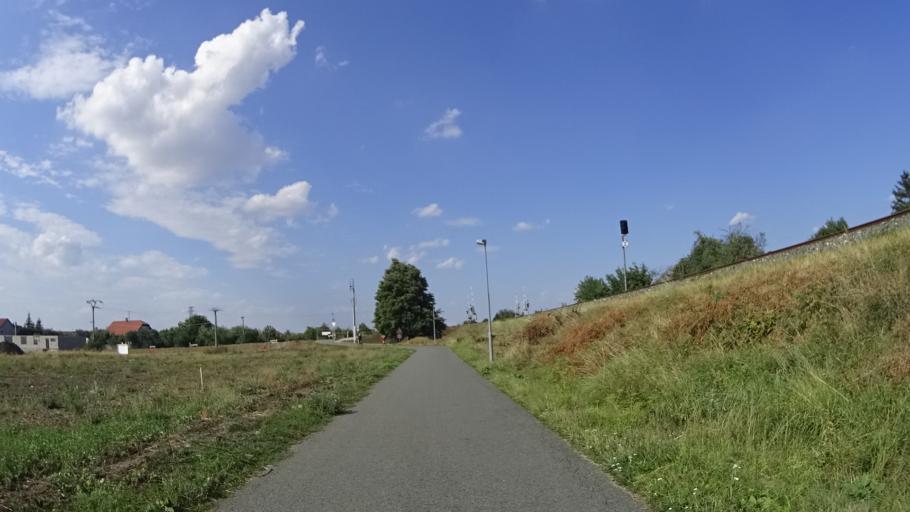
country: CZ
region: Zlin
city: Kunovice
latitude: 49.0414
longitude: 17.4614
